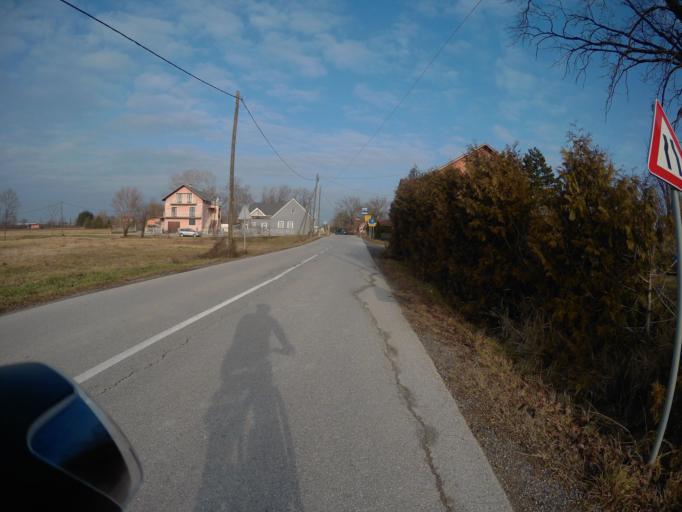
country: HR
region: Zagrebacka
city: Micevec
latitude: 45.7492
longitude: 16.1124
